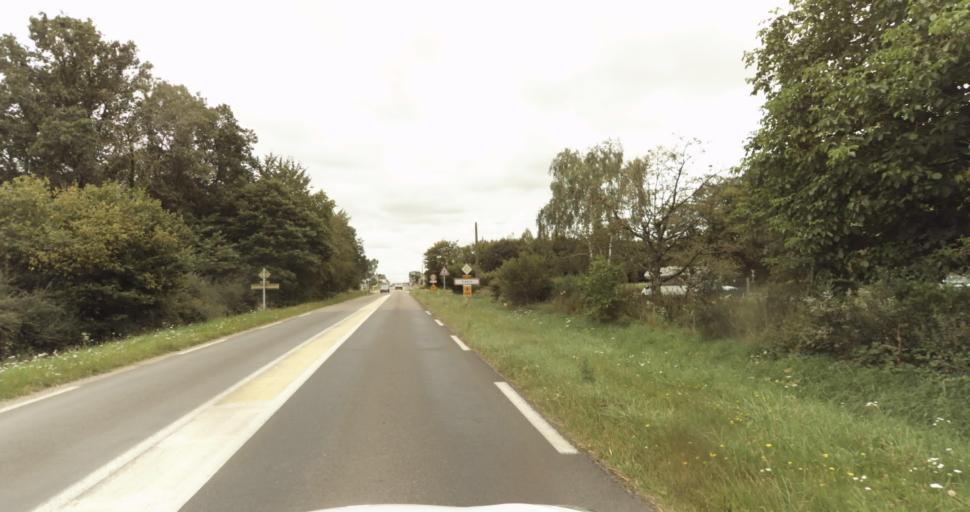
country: FR
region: Haute-Normandie
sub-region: Departement de l'Eure
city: La Madeleine-de-Nonancourt
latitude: 48.8202
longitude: 1.1864
